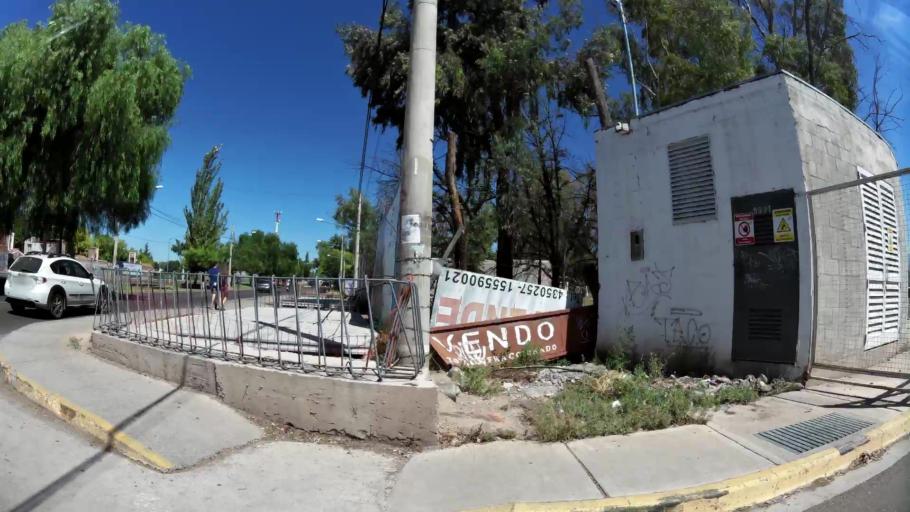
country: AR
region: Mendoza
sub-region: Departamento de Godoy Cruz
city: Godoy Cruz
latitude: -32.9527
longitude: -68.8559
